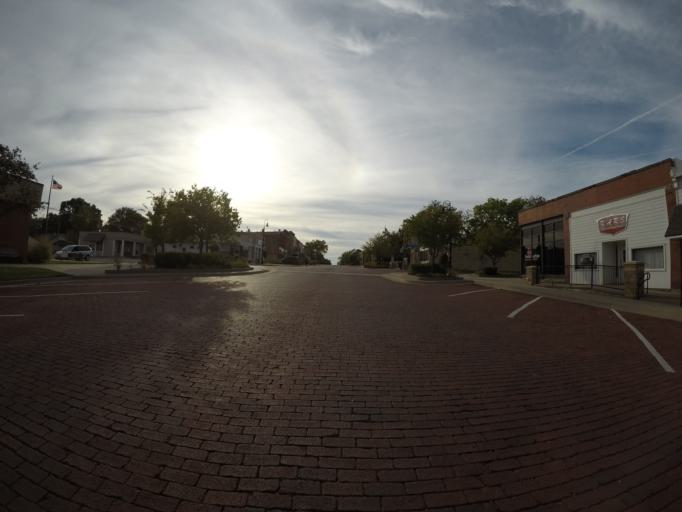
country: US
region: Kansas
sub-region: Douglas County
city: Baldwin City
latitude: 38.7749
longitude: -95.1871
